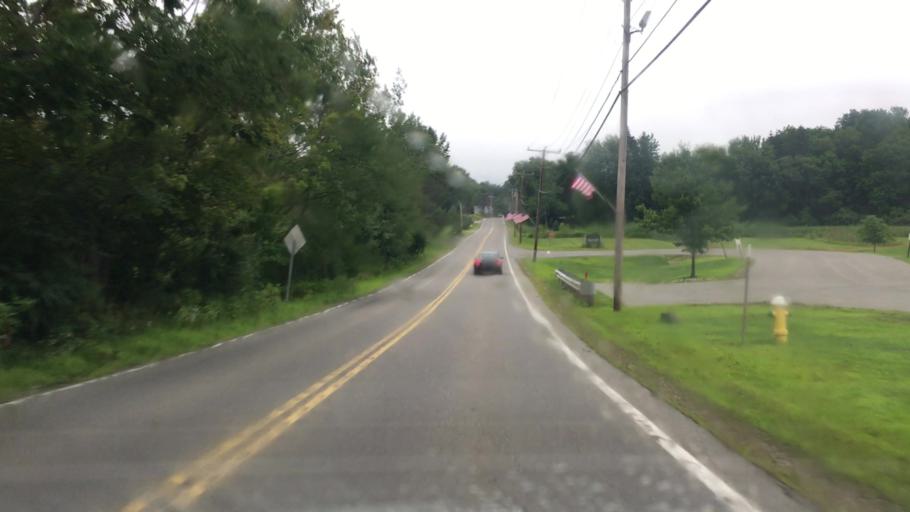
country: US
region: Maine
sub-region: York County
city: South Eliot
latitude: 43.1070
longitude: -70.8294
